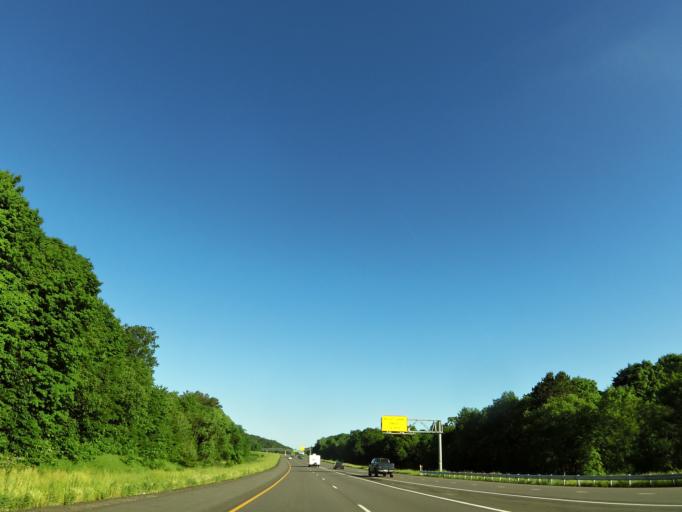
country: US
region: Minnesota
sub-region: Stearns County
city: Collegeville
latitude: 45.5857
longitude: -94.3615
